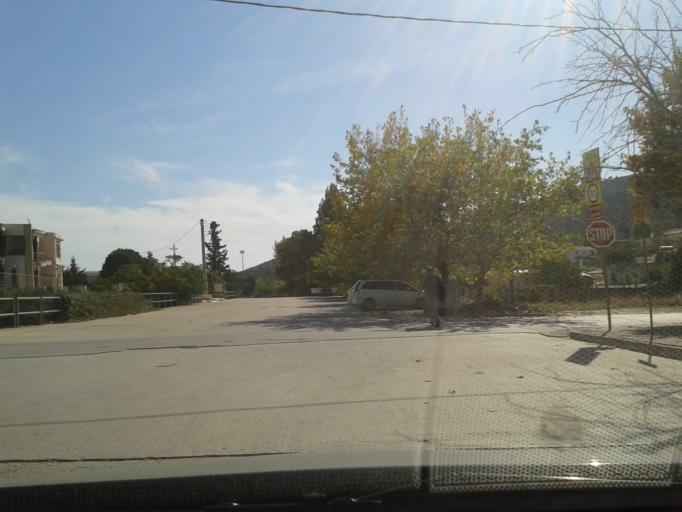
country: GR
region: Attica
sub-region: Nomarchia Anatolikis Attikis
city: Marathonas
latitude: 38.1568
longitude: 23.9591
